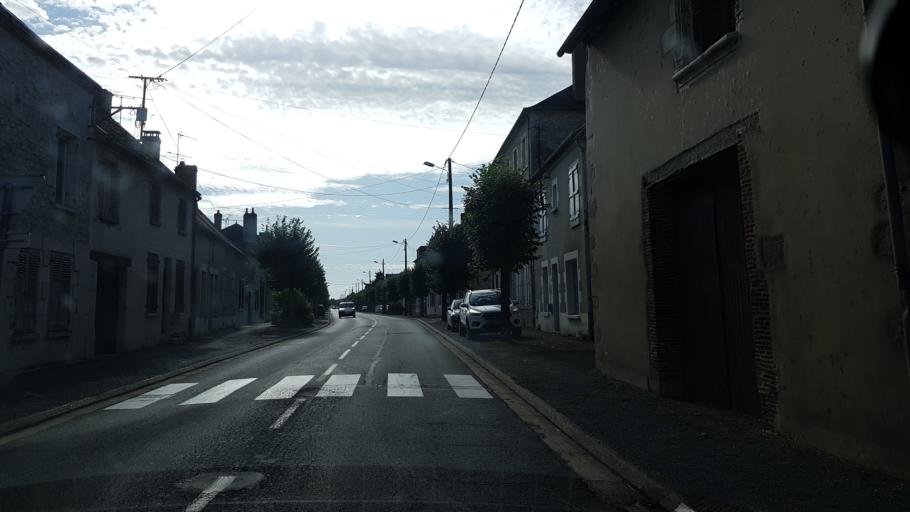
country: FR
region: Centre
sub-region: Departement du Loiret
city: Bonny-sur-Loire
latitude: 47.5586
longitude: 2.8408
